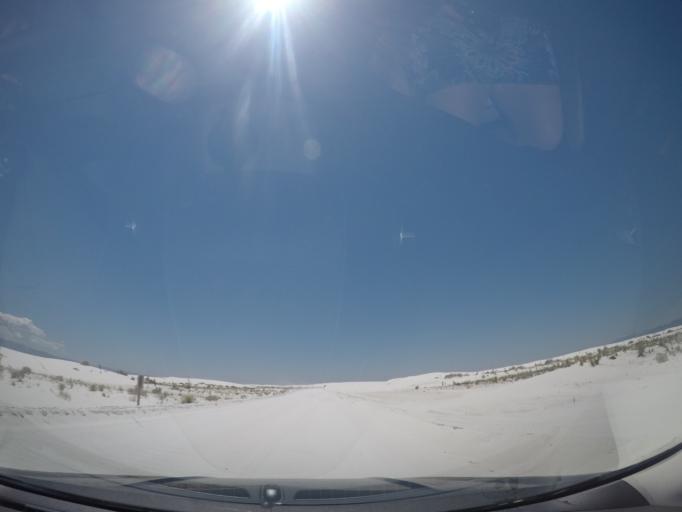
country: US
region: New Mexico
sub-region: Otero County
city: Holloman Air Force Base
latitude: 32.8057
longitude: -106.2603
